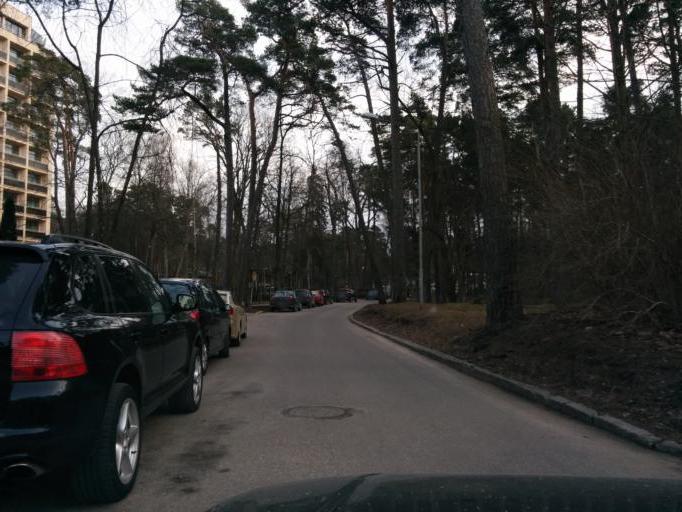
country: LV
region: Jurmala
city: Jurmala
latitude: 56.9816
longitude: 23.8394
